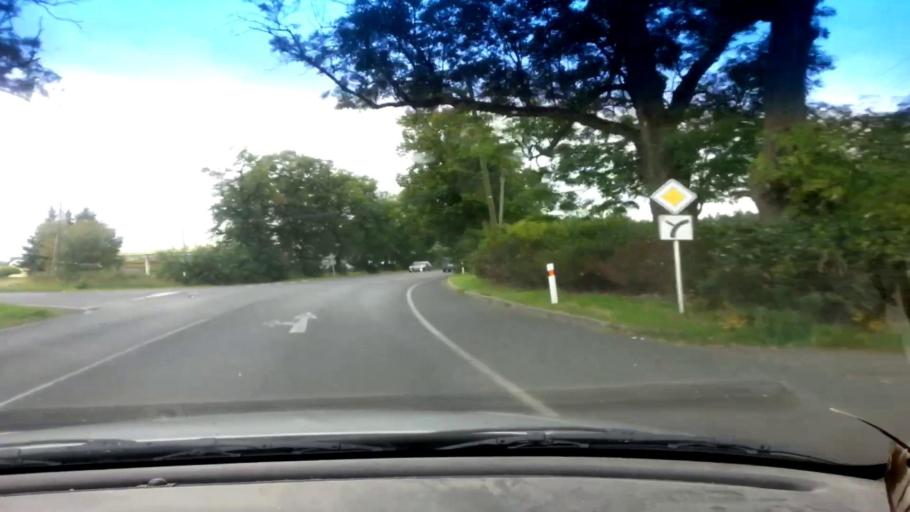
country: CZ
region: Karlovarsky
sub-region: Okres Cheb
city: Cheb
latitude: 50.0489
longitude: 12.3539
